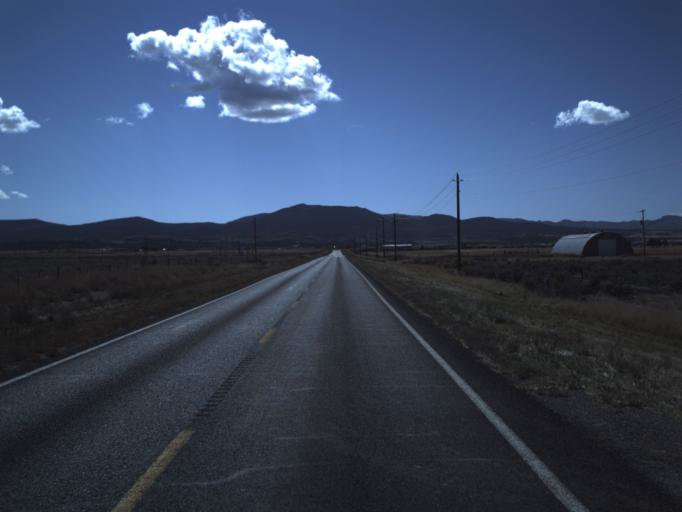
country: US
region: Utah
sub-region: Washington County
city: Enterprise
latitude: 37.6184
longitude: -113.6612
